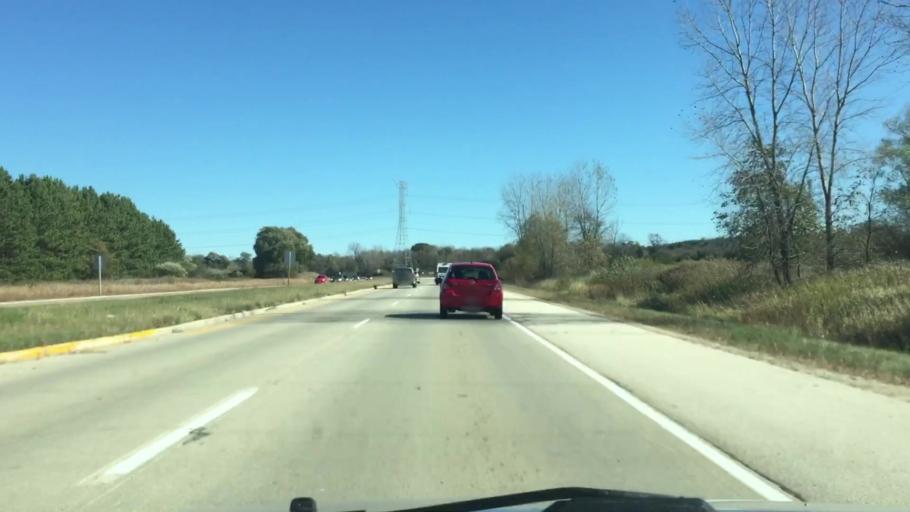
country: US
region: Wisconsin
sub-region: Waukesha County
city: Waukesha
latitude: 42.9796
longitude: -88.2174
